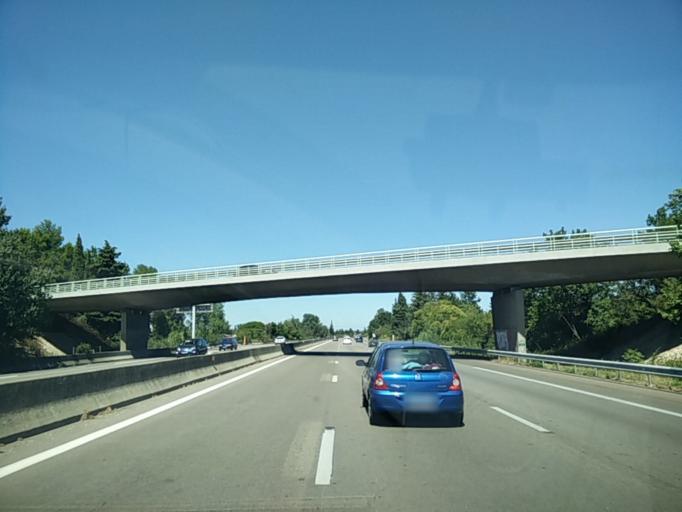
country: FR
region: Provence-Alpes-Cote d'Azur
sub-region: Departement du Vaucluse
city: Vedene
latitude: 43.9913
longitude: 4.8885
